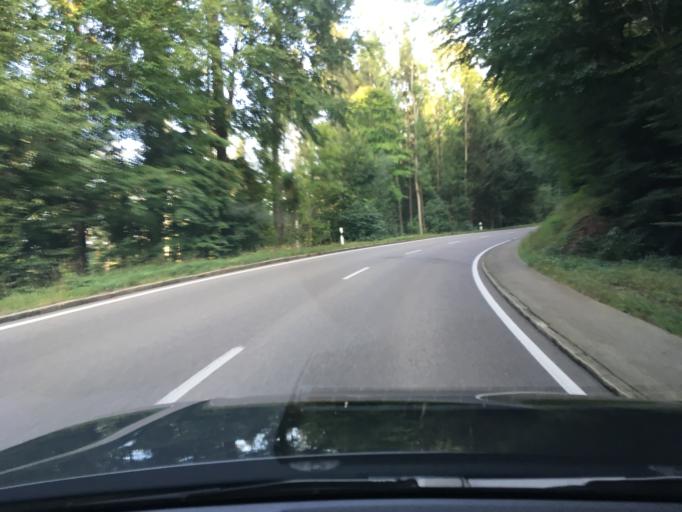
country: DE
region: Baden-Wuerttemberg
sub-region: Regierungsbezirk Stuttgart
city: Urbach
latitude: 48.7948
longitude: 9.5559
